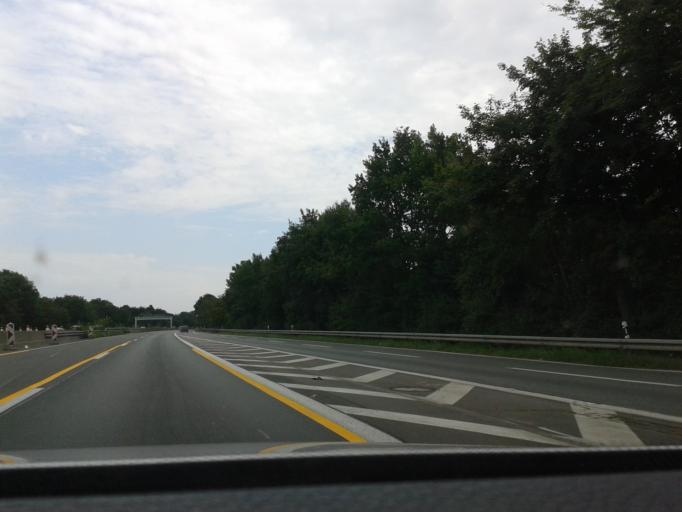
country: DE
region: North Rhine-Westphalia
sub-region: Regierungsbezirk Detmold
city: Wunnenberg
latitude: 51.5807
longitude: 8.7224
